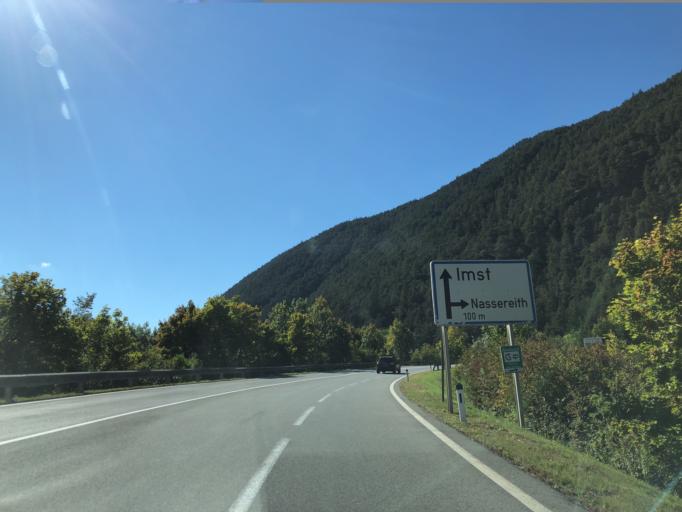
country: AT
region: Tyrol
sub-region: Politischer Bezirk Imst
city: Nassereith
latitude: 47.3029
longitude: 10.8394
